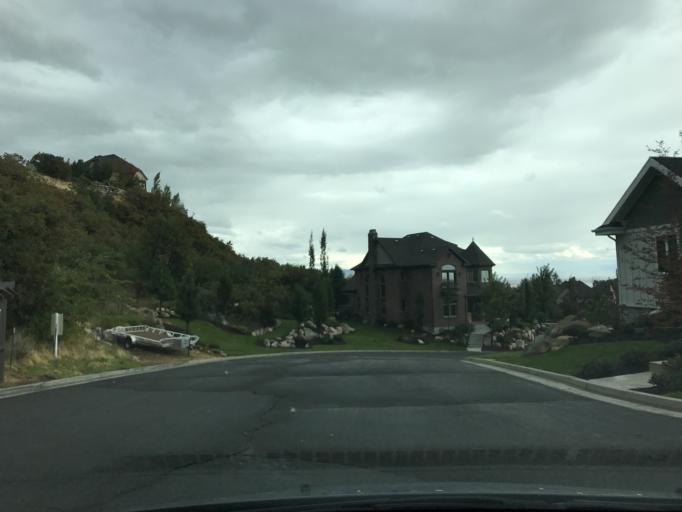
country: US
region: Utah
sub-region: Davis County
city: Fruit Heights
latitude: 41.0157
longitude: -111.8981
